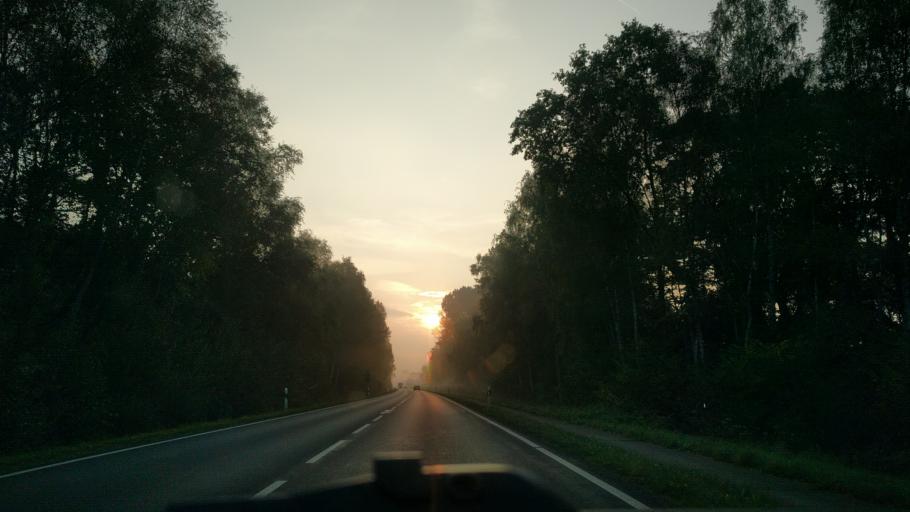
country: DE
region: Lower Saxony
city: Calberlah
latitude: 52.4370
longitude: 10.6121
